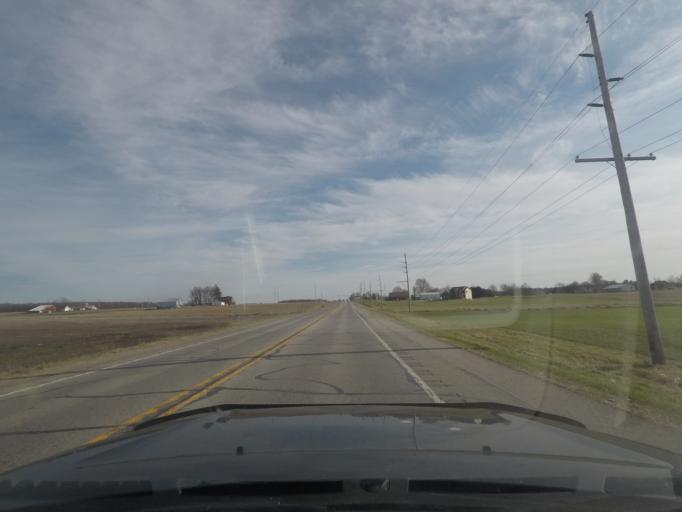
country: US
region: Indiana
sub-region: Elkhart County
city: Wakarusa
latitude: 41.4970
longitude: -86.0019
